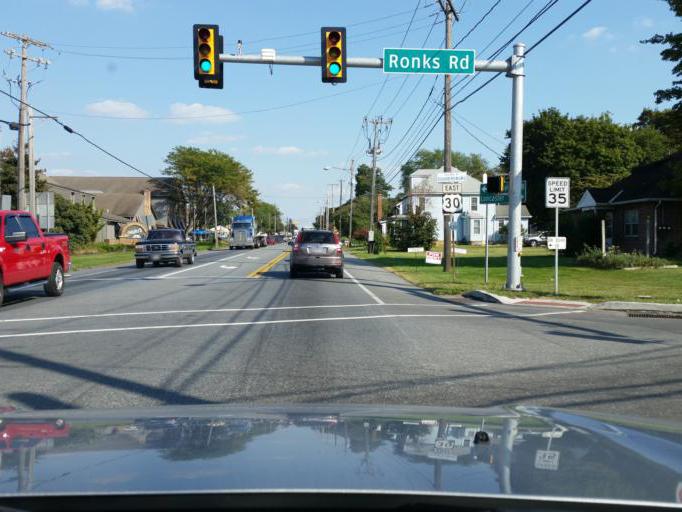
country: US
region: Pennsylvania
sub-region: Lancaster County
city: Paradise
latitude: 40.0169
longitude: -76.1651
